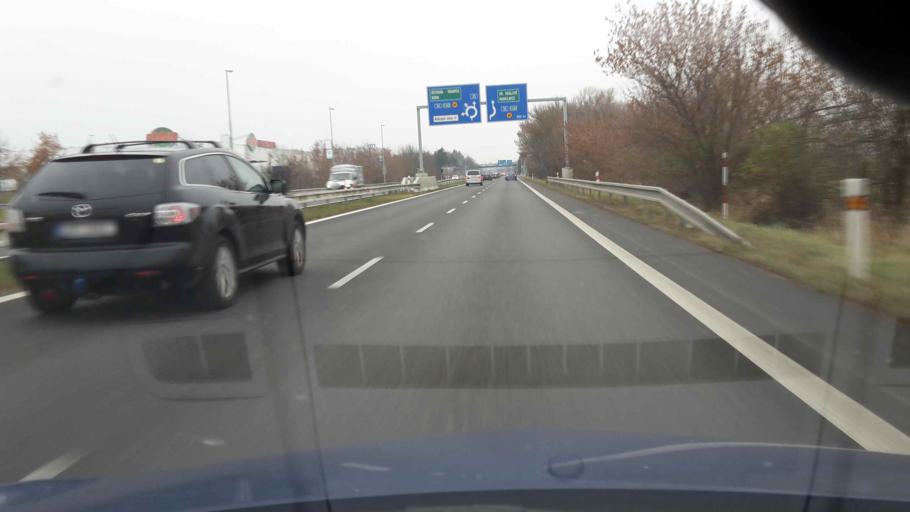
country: CZ
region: Olomoucky
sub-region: Okres Olomouc
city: Olomouc
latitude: 49.6010
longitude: 17.2272
